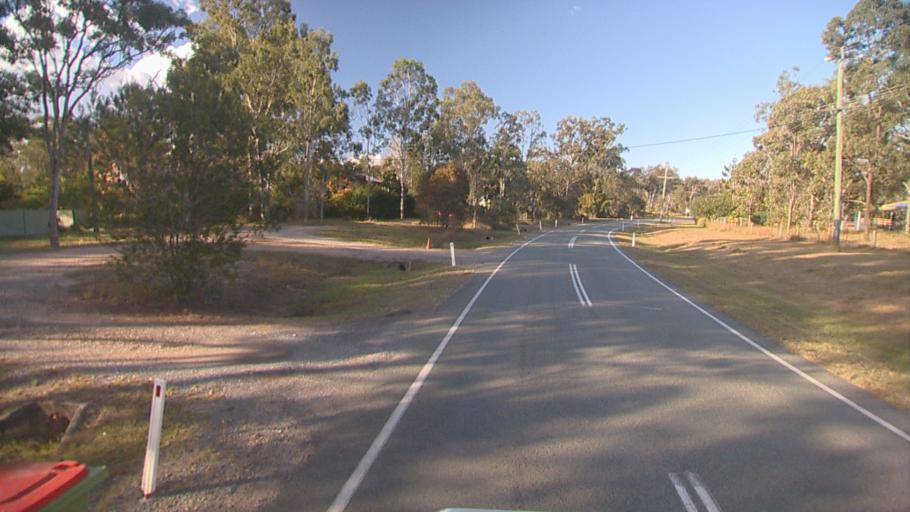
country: AU
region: Queensland
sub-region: Logan
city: Park Ridge South
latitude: -27.7173
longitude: 152.9717
